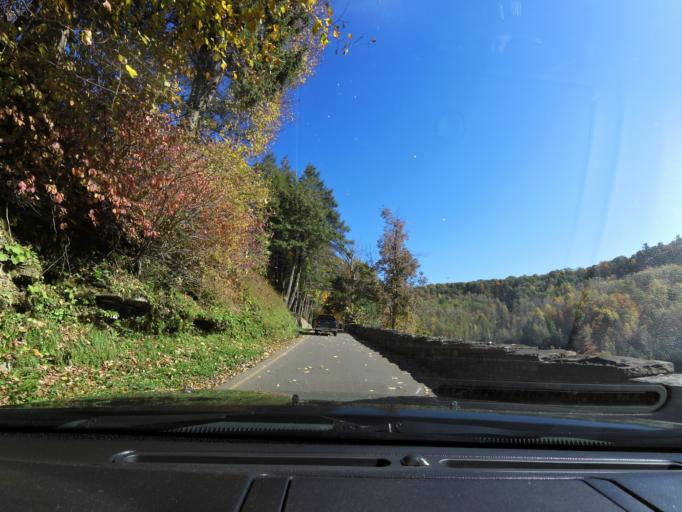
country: US
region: New York
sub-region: Wyoming County
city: Castile
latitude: 42.5839
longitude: -78.0430
